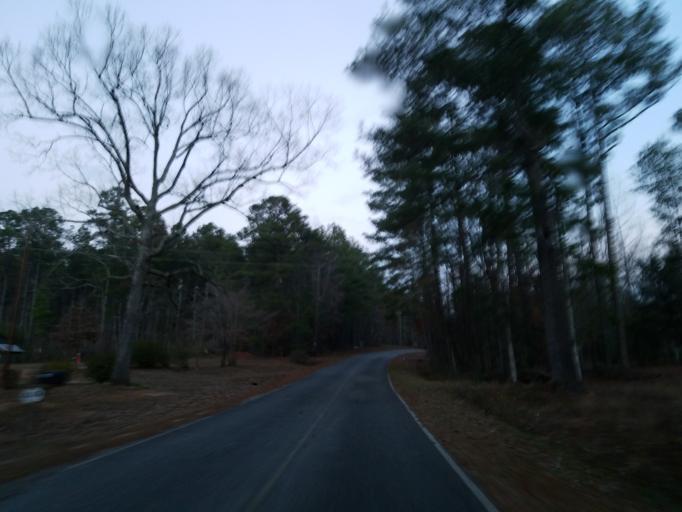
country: US
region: Alabama
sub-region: Sumter County
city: York
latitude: 32.4061
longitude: -88.4562
